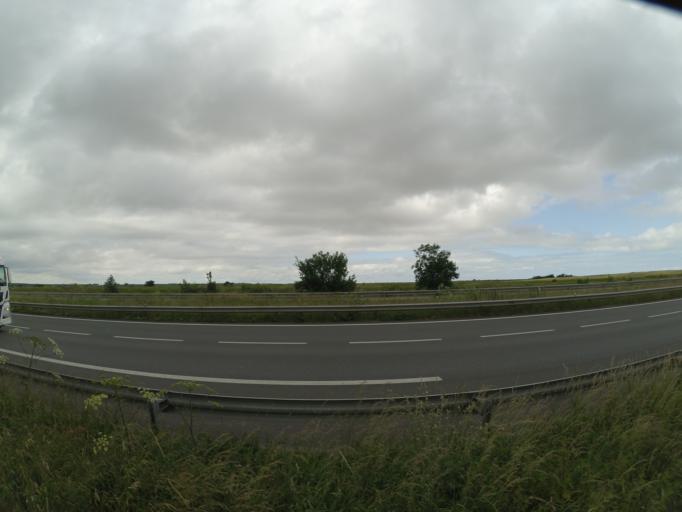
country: FR
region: Poitou-Charentes
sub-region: Departement de la Charente-Maritime
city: Yves
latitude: 46.0117
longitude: -1.0482
